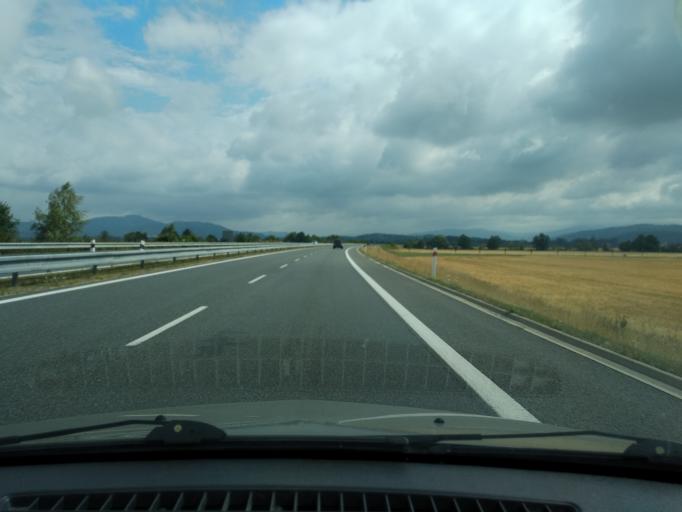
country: CZ
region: Olomoucky
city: Postrelmov
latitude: 49.9094
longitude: 16.8990
